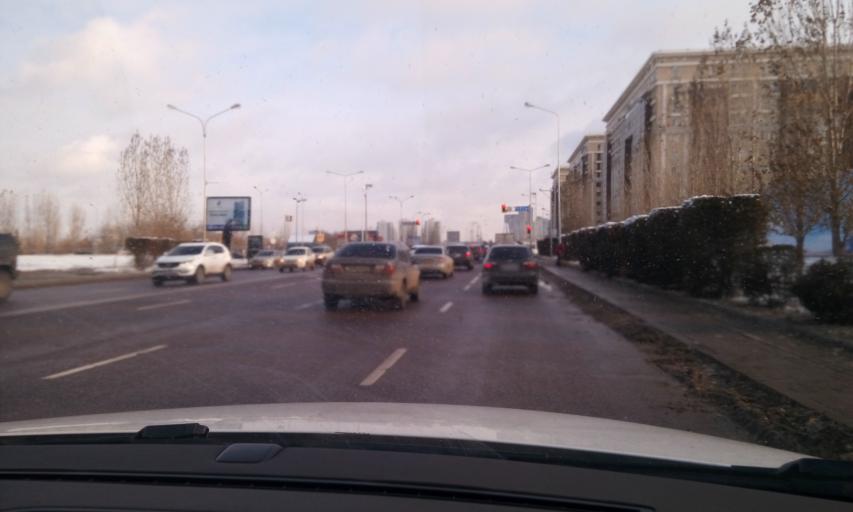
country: KZ
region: Astana Qalasy
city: Astana
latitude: 51.1336
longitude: 71.4325
